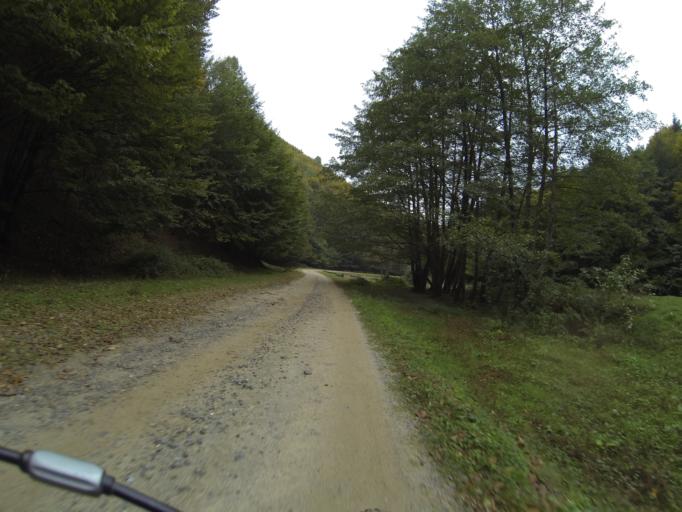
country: RO
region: Gorj
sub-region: Comuna Tismana
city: Sohodol
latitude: 45.0739
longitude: 22.8891
